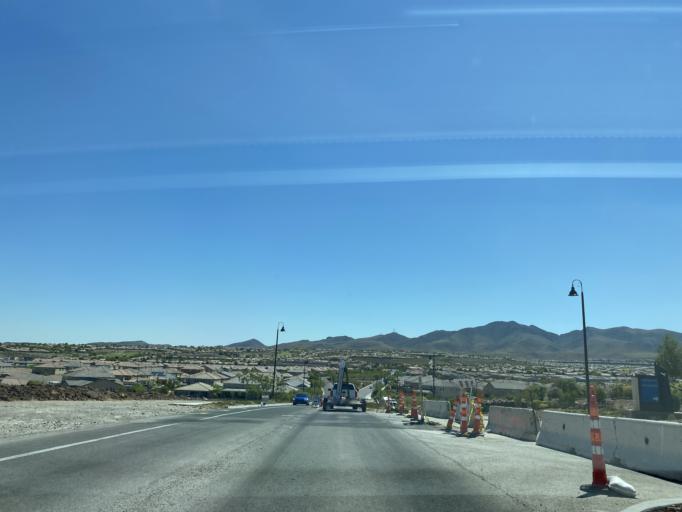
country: US
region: Nevada
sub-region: Clark County
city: Whitney
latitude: 35.9403
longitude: -115.1296
